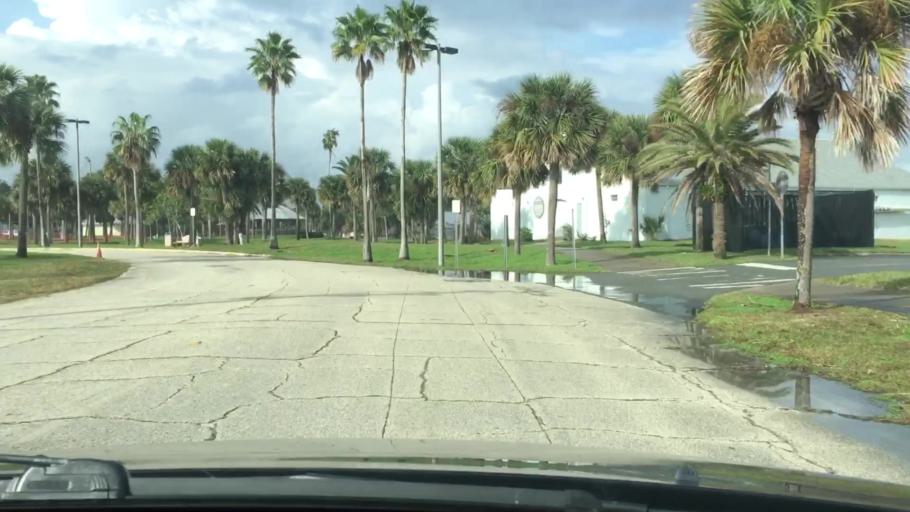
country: US
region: Florida
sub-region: Volusia County
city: Daytona Beach
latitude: 29.2106
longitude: -81.0149
